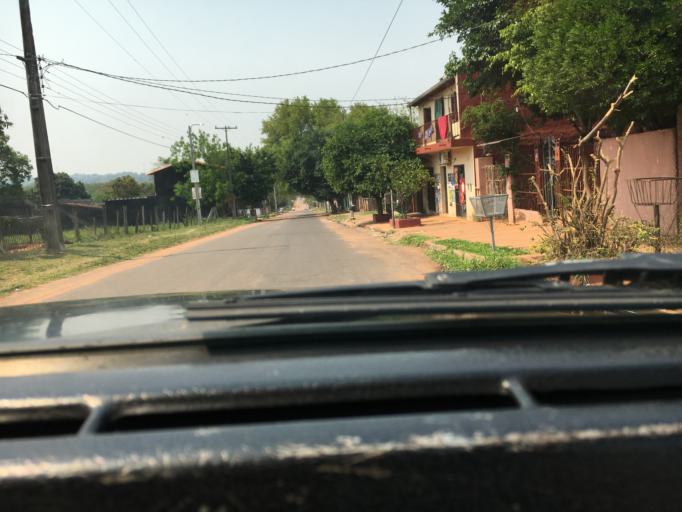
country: PY
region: Central
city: Villa Elisa
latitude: -25.3839
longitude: -57.5762
